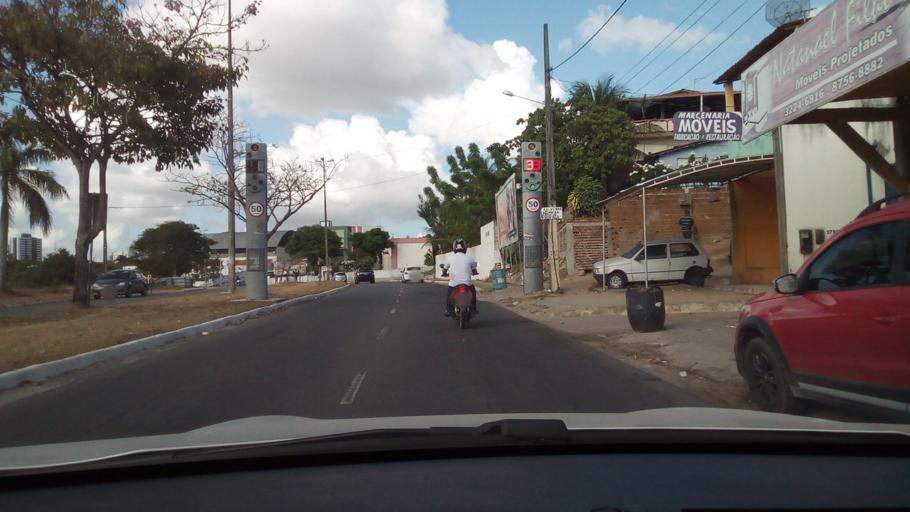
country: BR
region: Paraiba
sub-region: Joao Pessoa
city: Joao Pessoa
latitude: -7.1271
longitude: -34.8515
